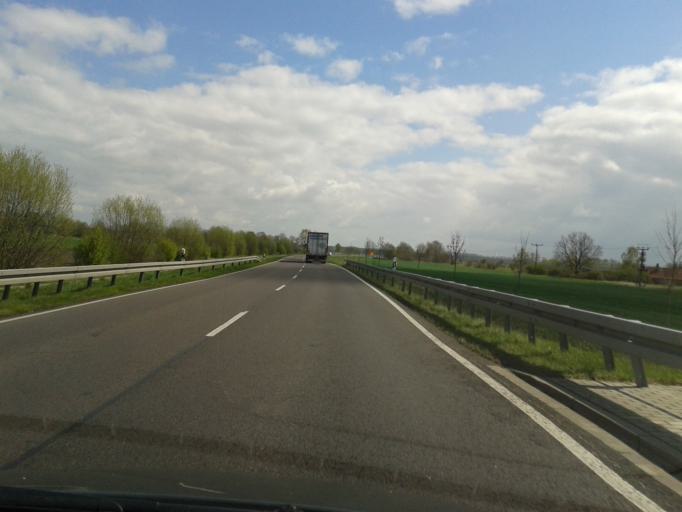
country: DE
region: Saxony-Anhalt
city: Salzwedel
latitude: 52.8682
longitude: 11.1684
